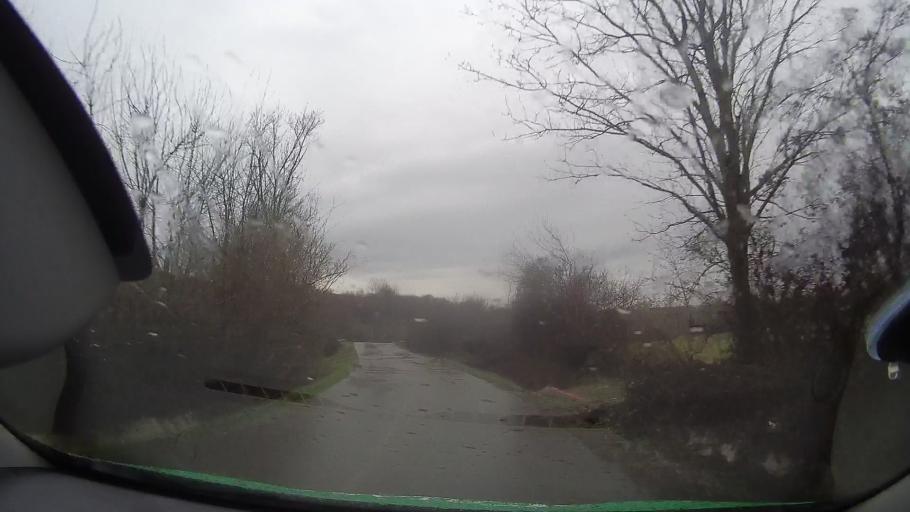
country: RO
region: Bihor
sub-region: Comuna Holod
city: Vintere
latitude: 46.7441
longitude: 22.1353
